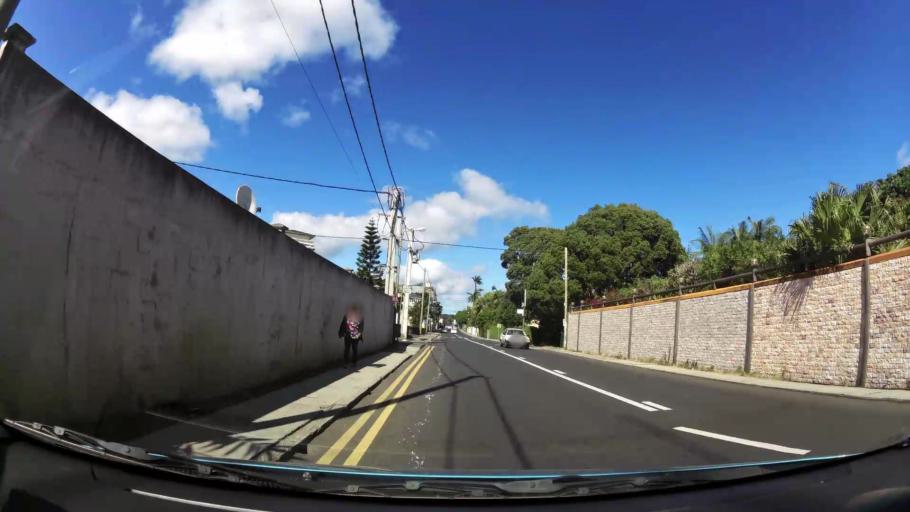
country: MU
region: Plaines Wilhems
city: Vacoas
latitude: -20.3013
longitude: 57.4926
